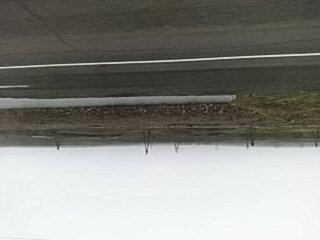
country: RU
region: Krasnoyarskiy
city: Kayyerkan
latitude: 69.3160
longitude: 87.9602
